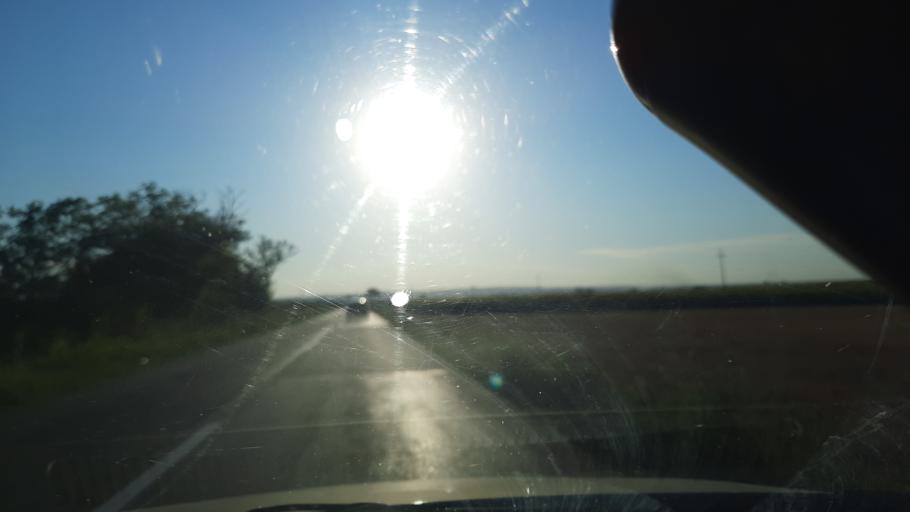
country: RS
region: Central Serbia
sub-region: Branicevski Okrug
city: Malo Crnice
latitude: 44.5826
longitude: 21.3064
